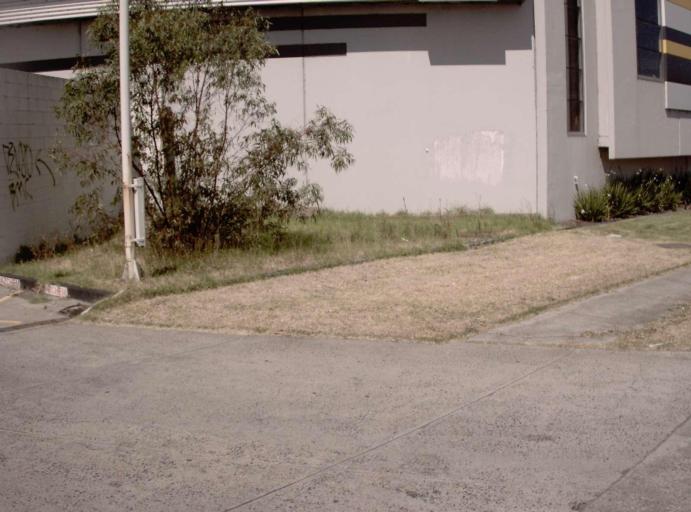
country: AU
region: Victoria
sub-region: Manningham
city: Bulleen
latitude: -37.7607
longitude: 145.0818
